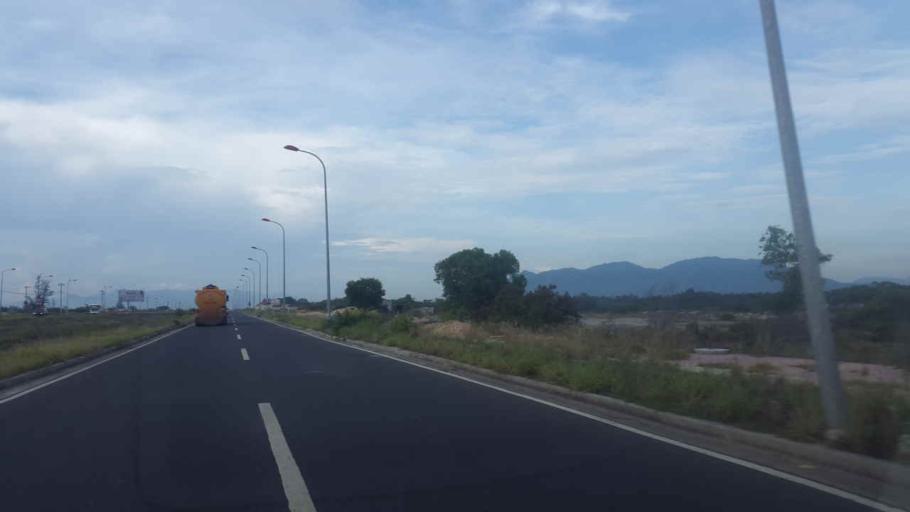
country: VN
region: Khanh Hoa
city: Cam Lam
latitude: 12.0146
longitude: 109.2125
